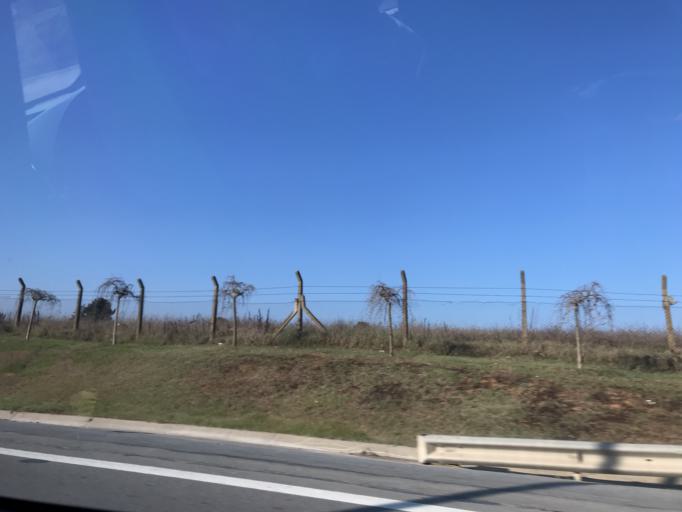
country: TR
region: Istanbul
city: Sultanbeyli
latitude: 40.9339
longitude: 29.3462
